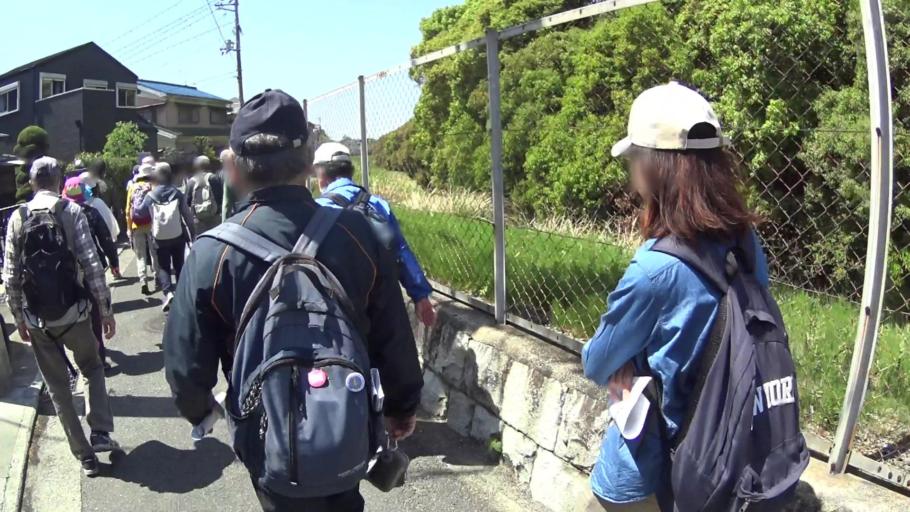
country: JP
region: Osaka
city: Kashihara
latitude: 34.5700
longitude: 135.6141
